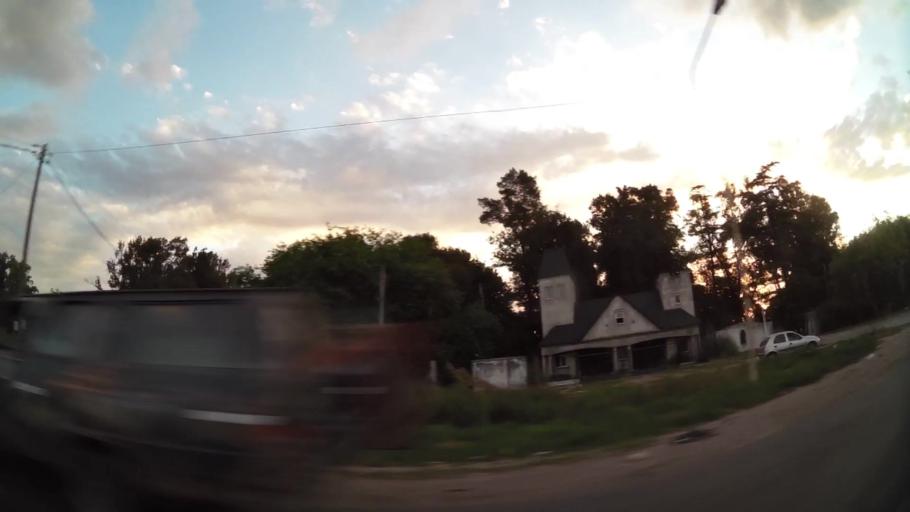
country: AR
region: Buenos Aires
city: Santa Catalina - Dique Lujan
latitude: -34.4761
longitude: -58.7847
